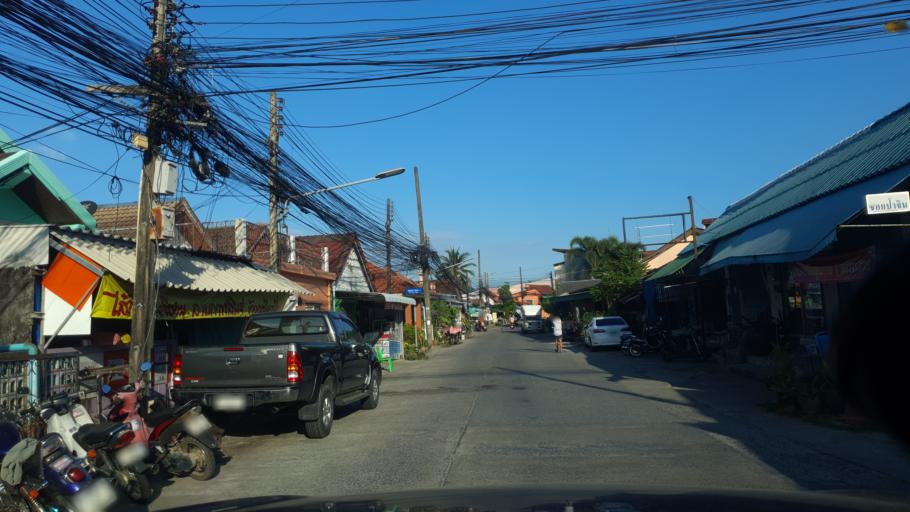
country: TH
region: Phuket
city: Kathu
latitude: 7.9028
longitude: 98.3303
